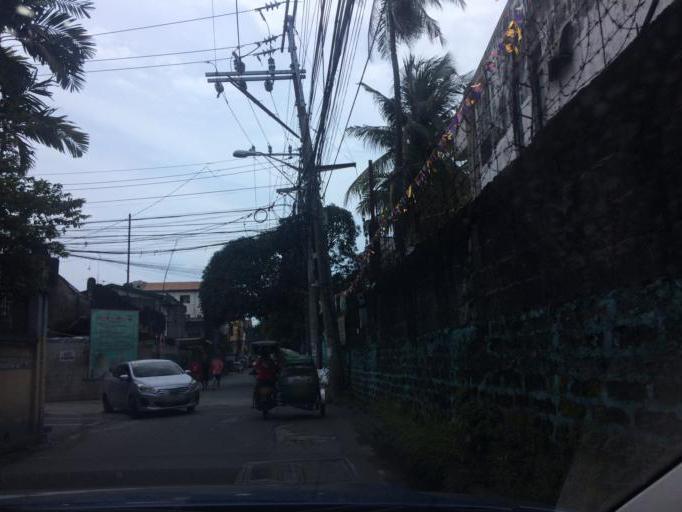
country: PH
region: Metro Manila
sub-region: Makati City
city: Makati City
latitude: 14.5432
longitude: 121.0039
